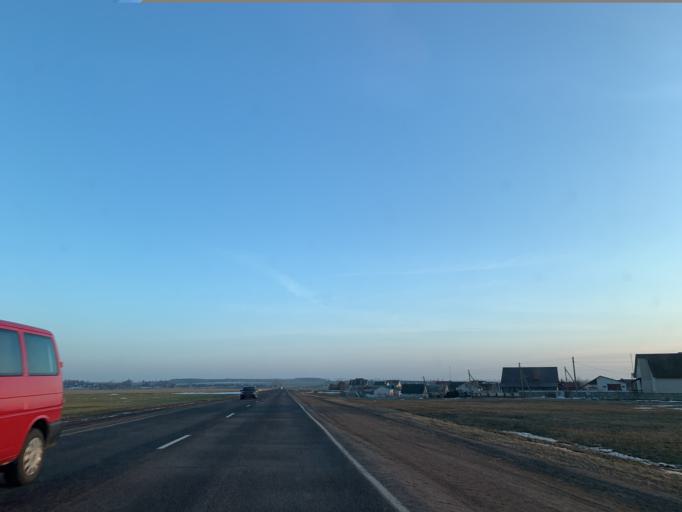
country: BY
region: Minsk
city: Haradzyeya
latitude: 53.3140
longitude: 26.5640
